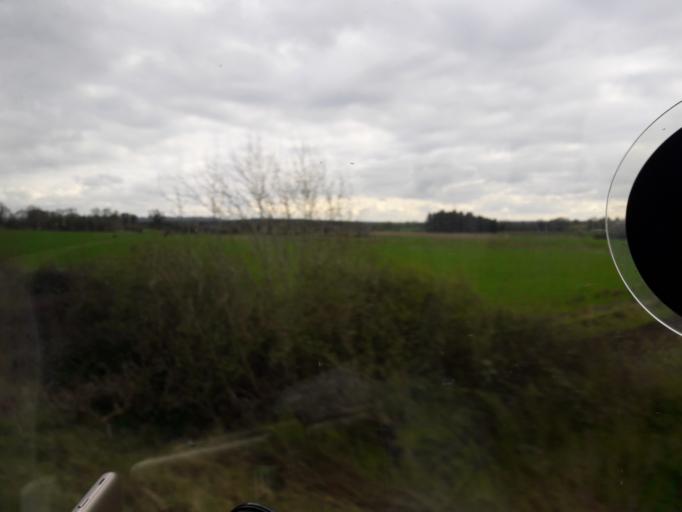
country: IE
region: Leinster
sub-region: An Longfort
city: Granard
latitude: 53.6686
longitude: -7.4931
